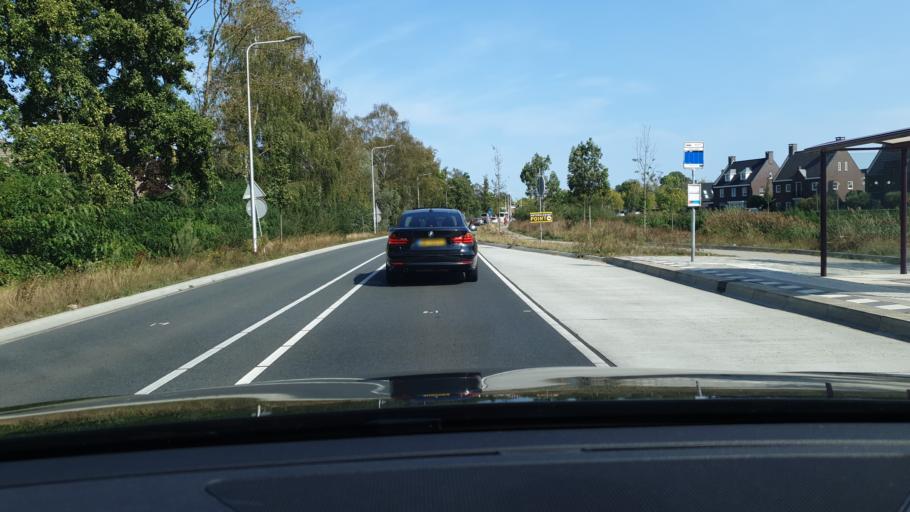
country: NL
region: North Brabant
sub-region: Gemeente Laarbeek
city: Aarle-Rixtel
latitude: 51.5272
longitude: 5.6362
